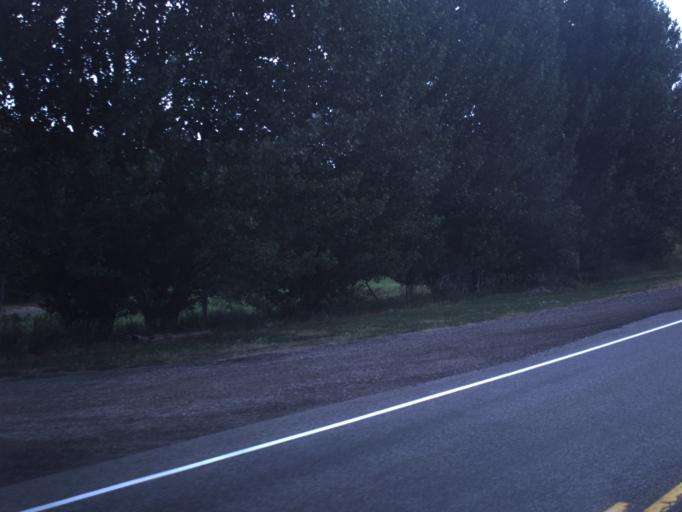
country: US
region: Utah
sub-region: Sanpete County
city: Fountain Green
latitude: 39.7118
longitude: -111.7186
